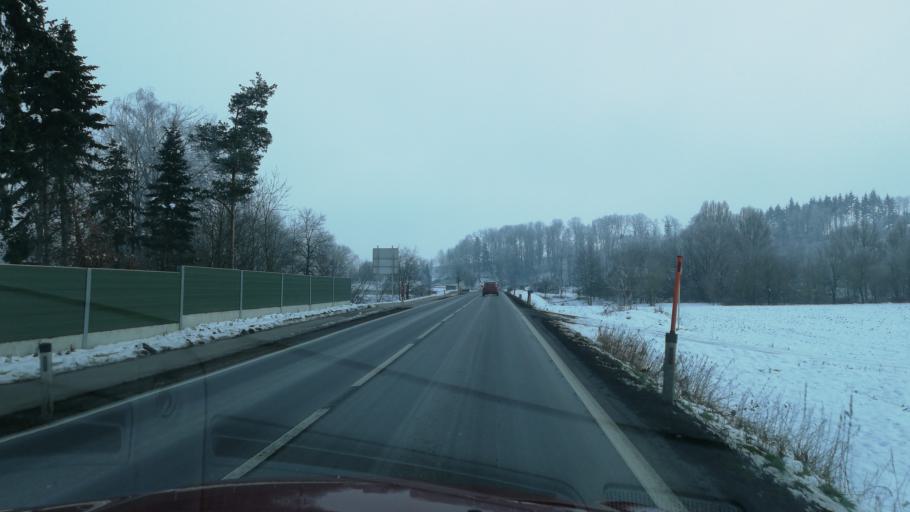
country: AT
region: Upper Austria
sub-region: Politischer Bezirk Grieskirchen
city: Bad Schallerbach
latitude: 48.2364
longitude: 13.9591
